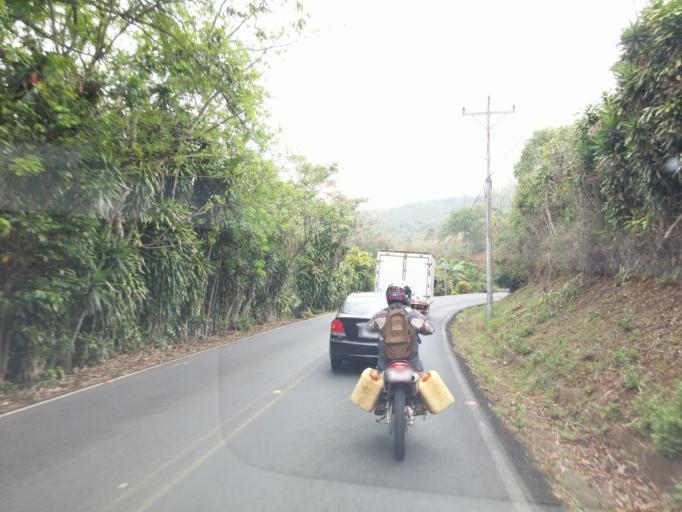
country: CR
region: Alajuela
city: San Ramon
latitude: 10.1191
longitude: -84.4711
